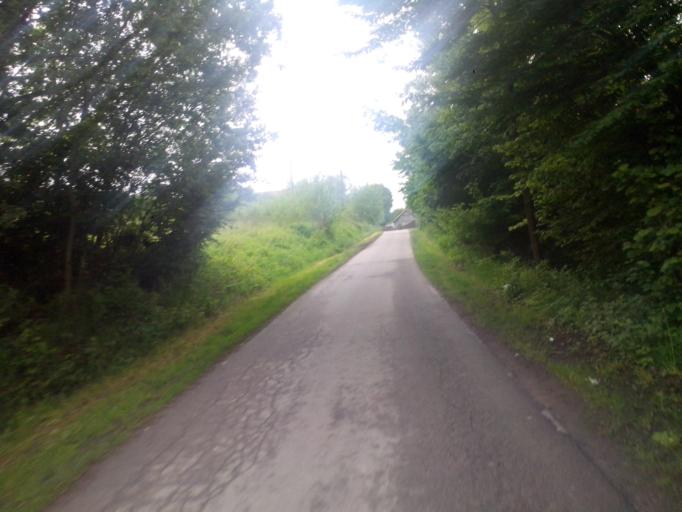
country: PL
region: Subcarpathian Voivodeship
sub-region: Powiat strzyzowski
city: Strzyzow
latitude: 49.8690
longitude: 21.8091
